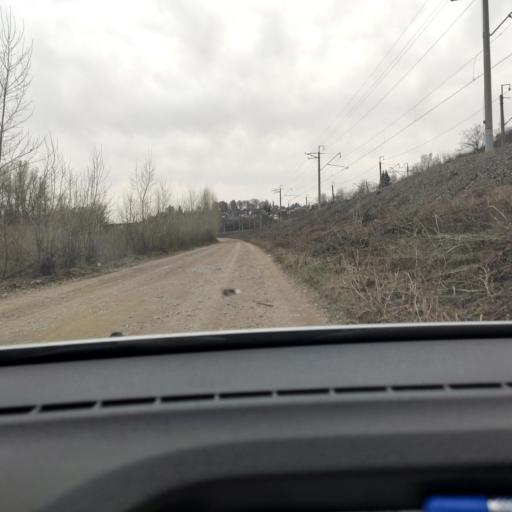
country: RU
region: Bashkortostan
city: Avdon
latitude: 54.6157
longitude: 55.6063
